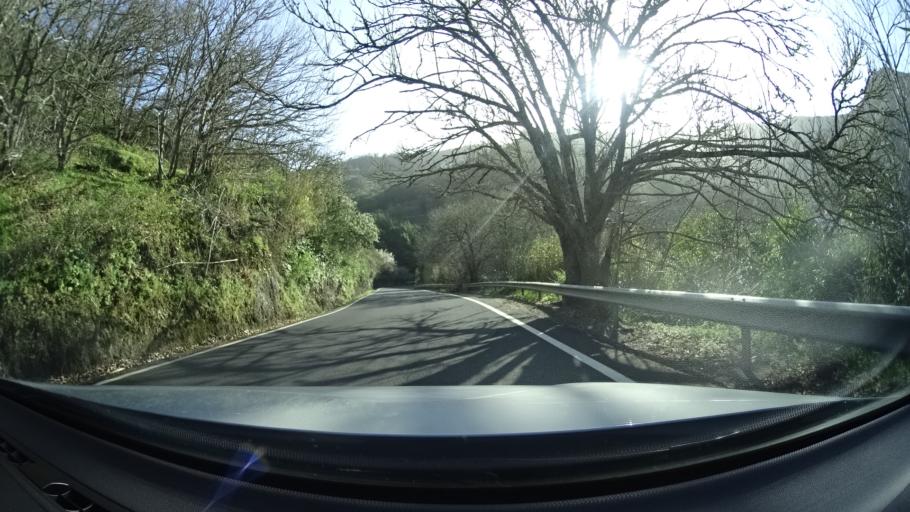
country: ES
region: Canary Islands
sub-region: Provincia de Las Palmas
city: Valleseco
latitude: 28.0296
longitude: -15.5593
